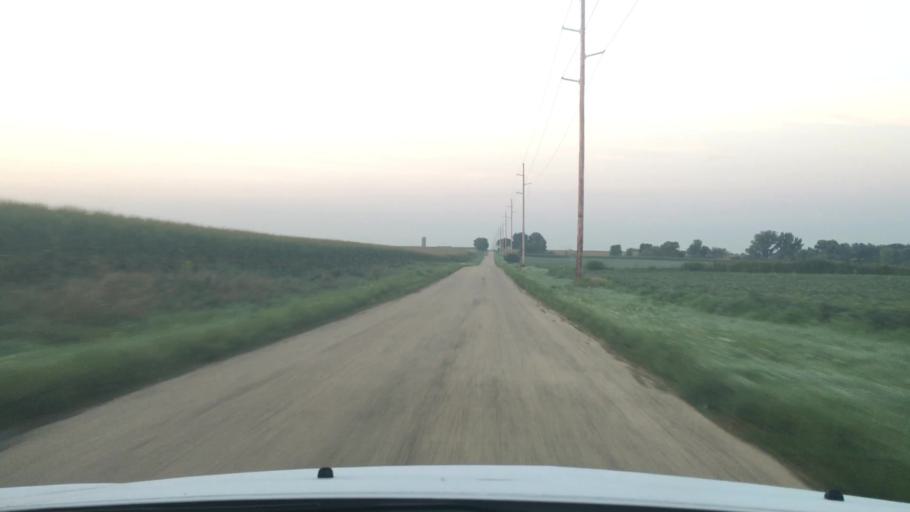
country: US
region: Illinois
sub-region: Ogle County
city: Rochelle
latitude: 41.8707
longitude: -89.0008
